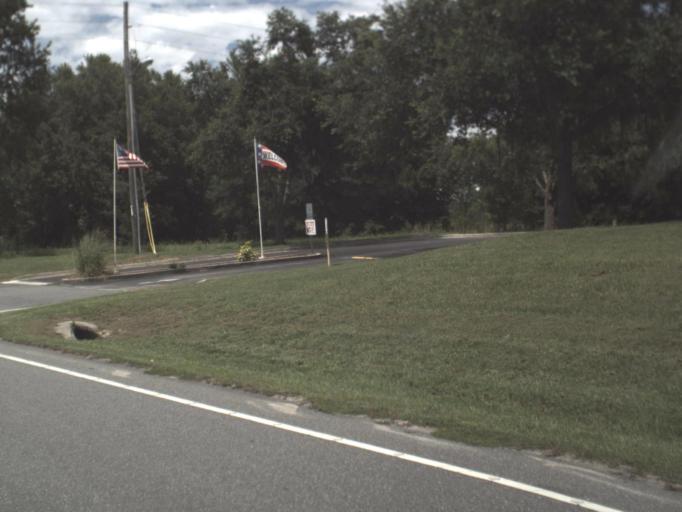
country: US
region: Florida
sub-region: Citrus County
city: Hernando
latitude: 28.9146
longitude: -82.3755
